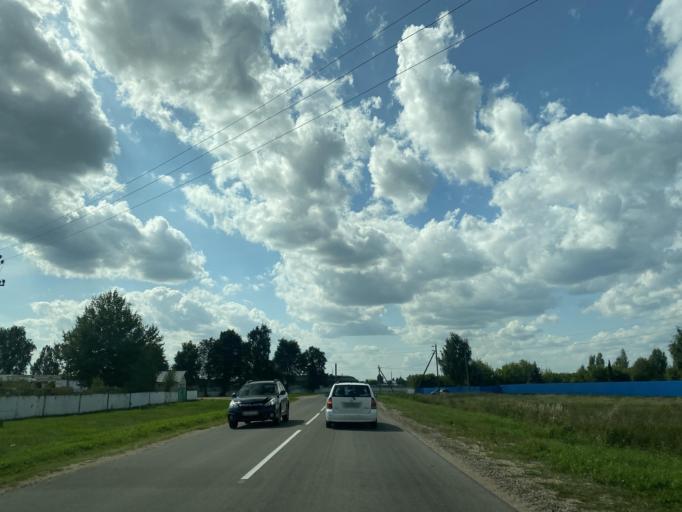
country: BY
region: Minsk
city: Horad Zhodzina
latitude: 54.0863
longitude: 28.3647
